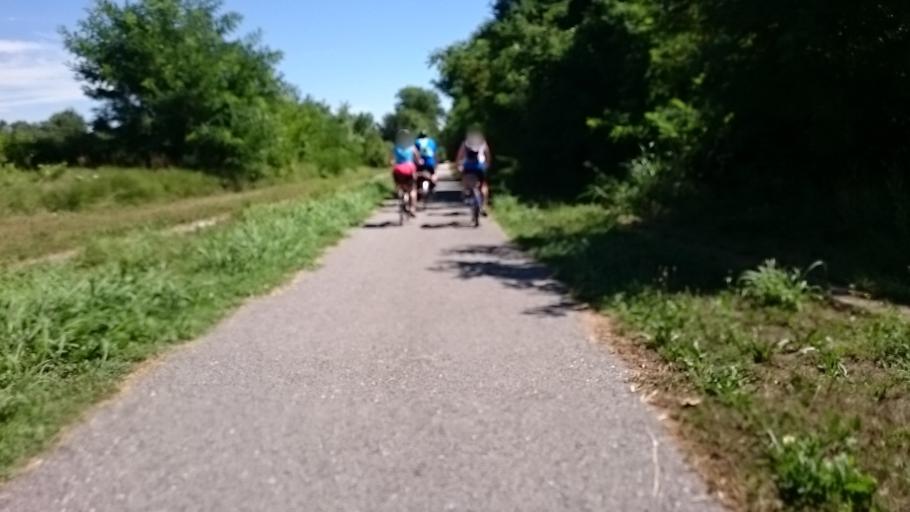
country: IT
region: Veneto
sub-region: Provincia di Treviso
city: Badoere
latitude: 45.6243
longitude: 12.0785
